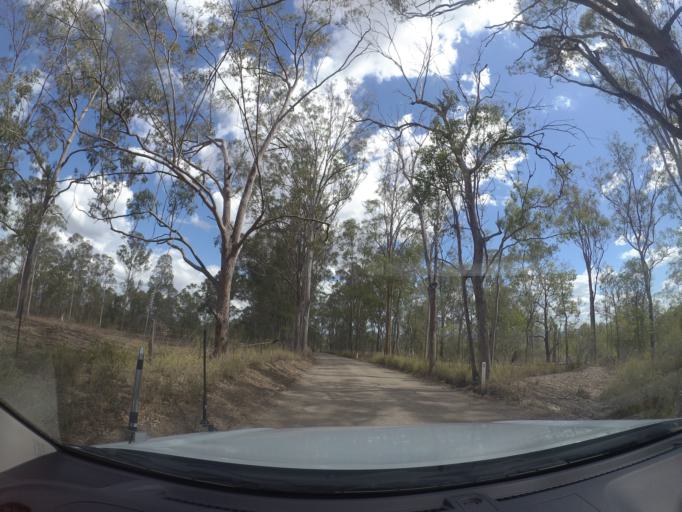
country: AU
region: Queensland
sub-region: Logan
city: Cedar Vale
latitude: -27.8997
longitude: 152.9873
